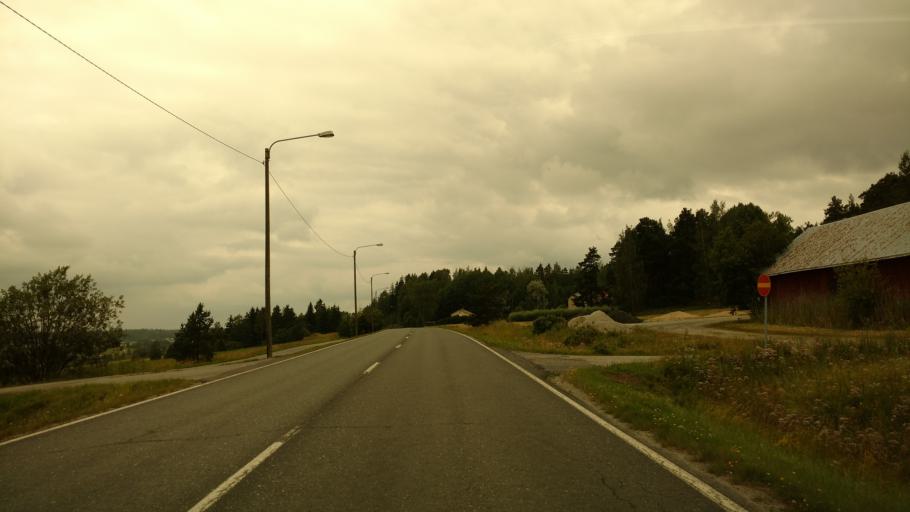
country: FI
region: Varsinais-Suomi
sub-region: Salo
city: Halikko
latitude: 60.4066
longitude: 23.0660
